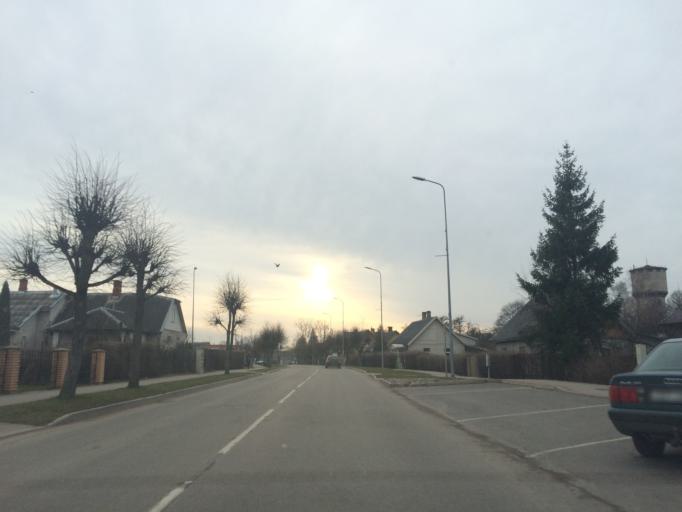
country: LV
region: Rezekne
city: Rezekne
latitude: 56.5115
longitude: 27.3399
